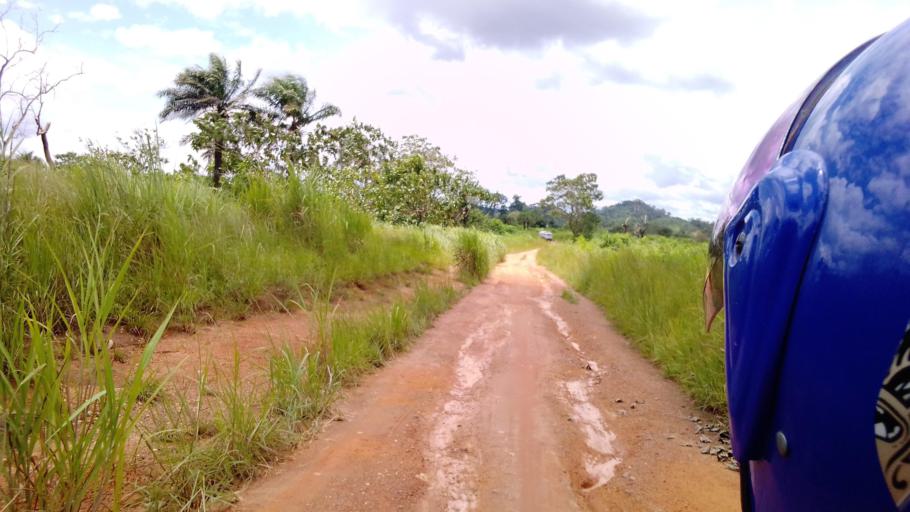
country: SL
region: Eastern Province
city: Koidu
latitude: 8.6707
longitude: -10.9535
